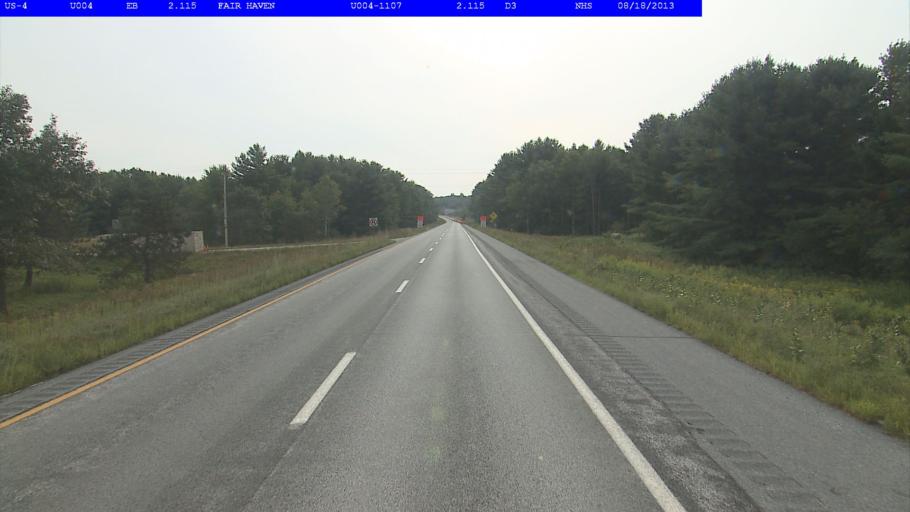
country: US
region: Vermont
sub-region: Rutland County
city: Fair Haven
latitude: 43.6055
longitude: -73.2692
